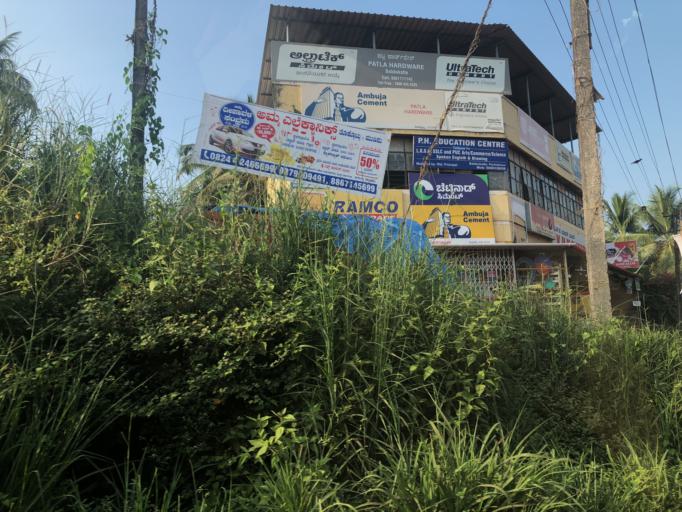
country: IN
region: Karnataka
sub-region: Dakshina Kannada
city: Ullal
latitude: 12.8190
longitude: 74.8670
